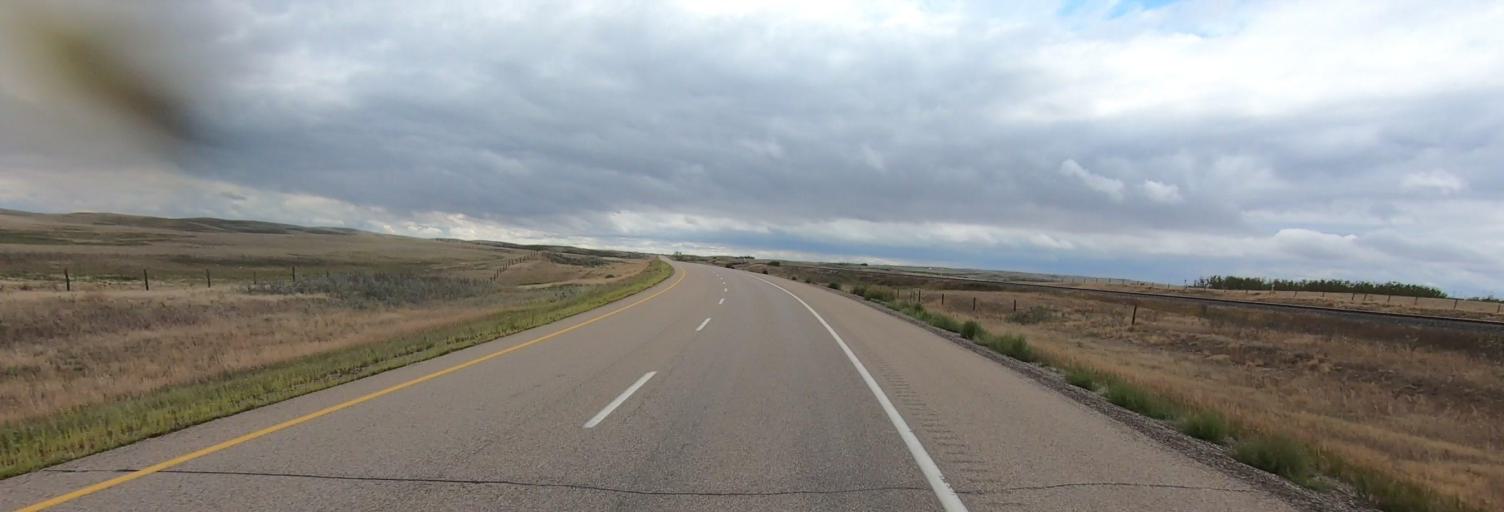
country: CA
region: Saskatchewan
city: Gravelbourg
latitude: 50.4806
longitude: -106.8474
